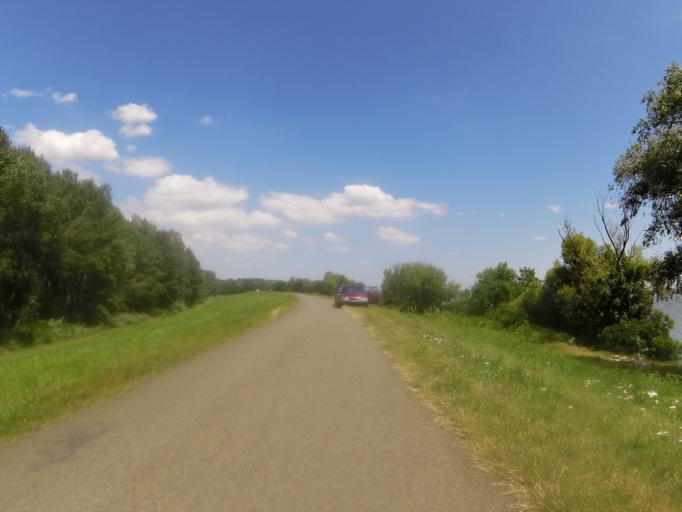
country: HU
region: Heves
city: Tiszanana
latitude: 47.5565
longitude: 20.6051
